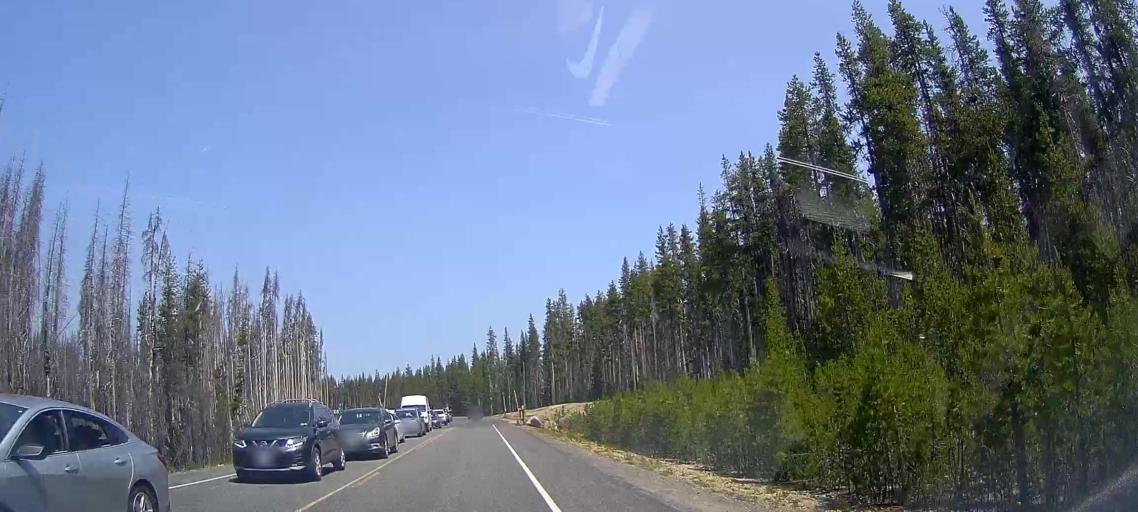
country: US
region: Oregon
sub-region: Lane County
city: Oakridge
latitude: 43.0862
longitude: -122.1165
